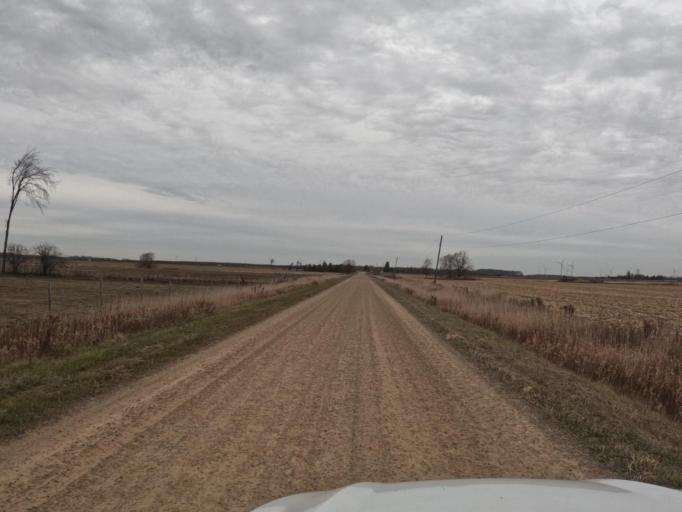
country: CA
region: Ontario
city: Shelburne
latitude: 44.0338
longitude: -80.3719
